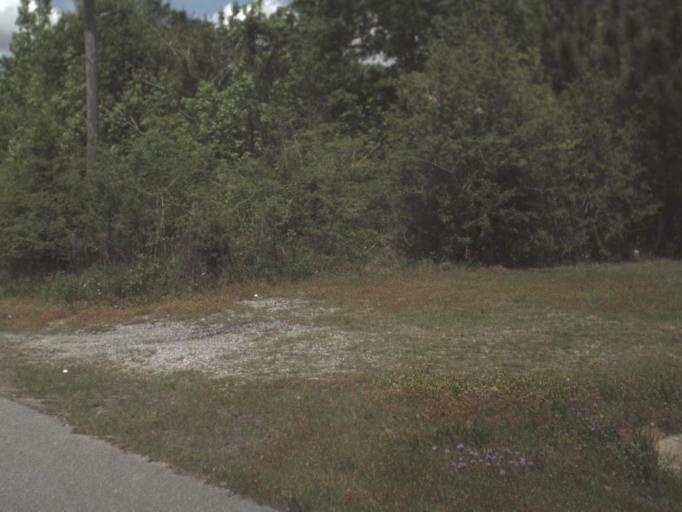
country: US
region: Florida
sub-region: Escambia County
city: Molino
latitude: 30.7294
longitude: -87.3469
